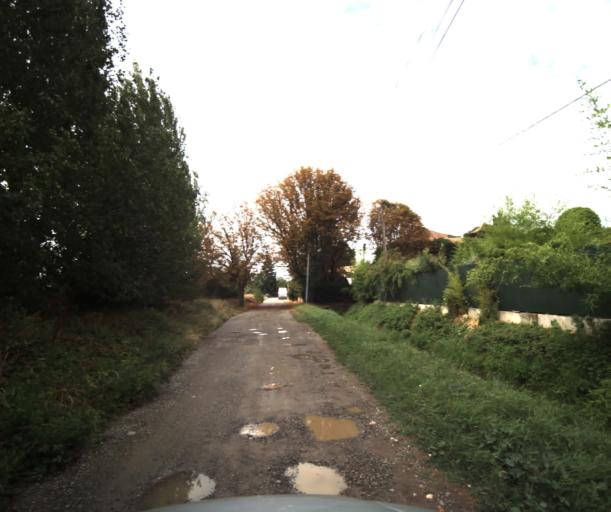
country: FR
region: Midi-Pyrenees
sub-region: Departement de la Haute-Garonne
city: Pinsaguel
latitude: 43.5267
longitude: 1.3749
